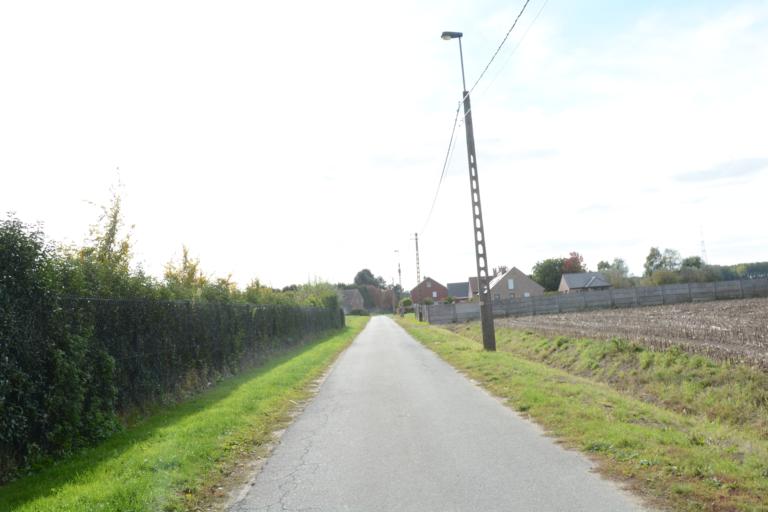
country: BE
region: Flanders
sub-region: Provincie Antwerpen
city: Sint-Amands
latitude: 51.0366
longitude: 4.2399
